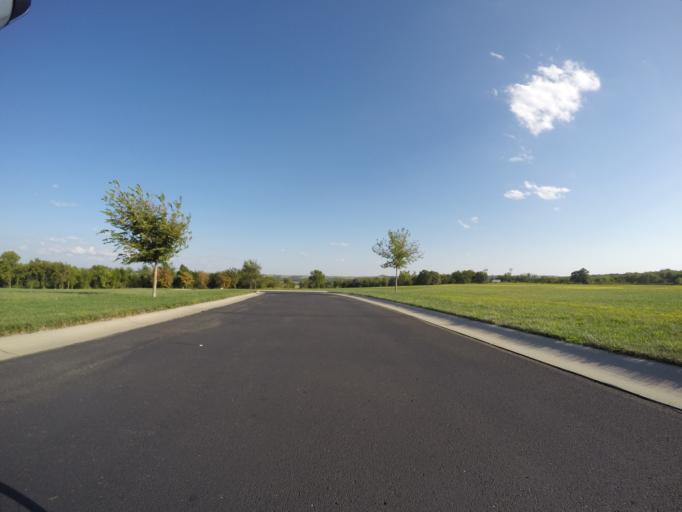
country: US
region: Kansas
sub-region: Riley County
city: Ogden
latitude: 39.1346
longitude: -96.6866
